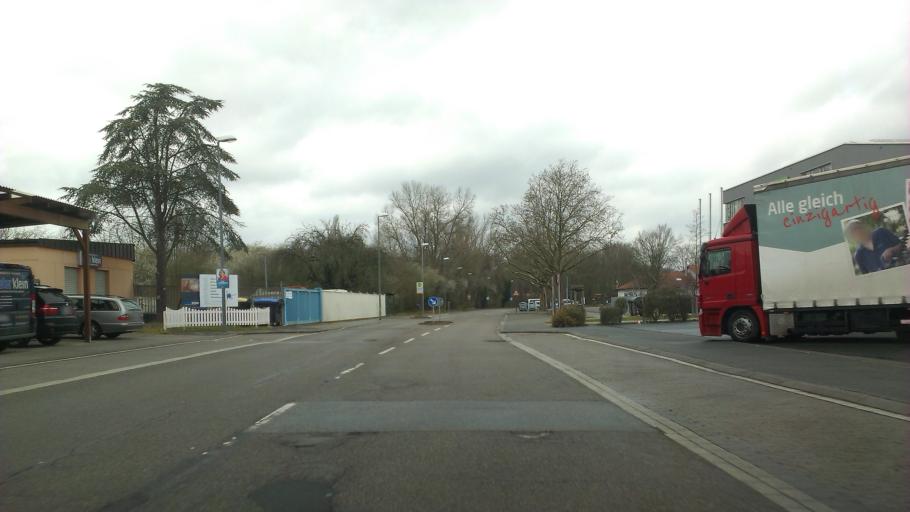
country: DE
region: Rheinland-Pfalz
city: Frankenthal
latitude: 49.5026
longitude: 8.3713
